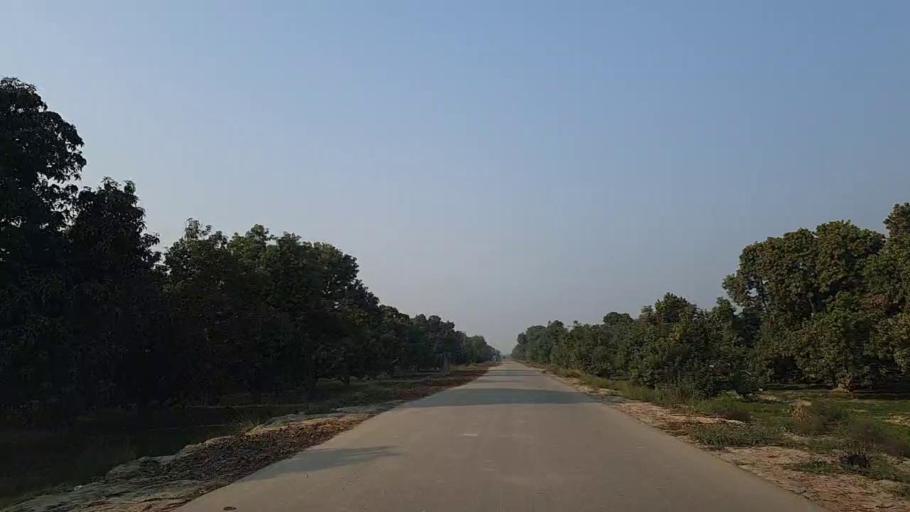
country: PK
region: Sindh
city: Sann
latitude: 26.1039
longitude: 68.1514
